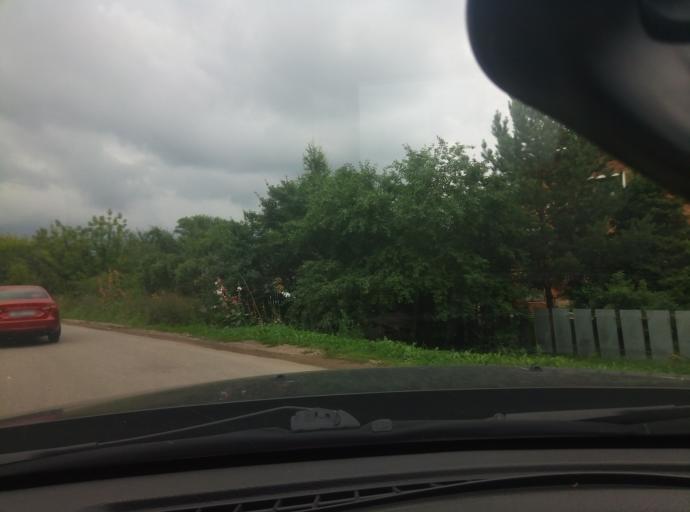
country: RU
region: Tula
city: Kimovsk
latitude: 53.9669
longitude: 38.5354
